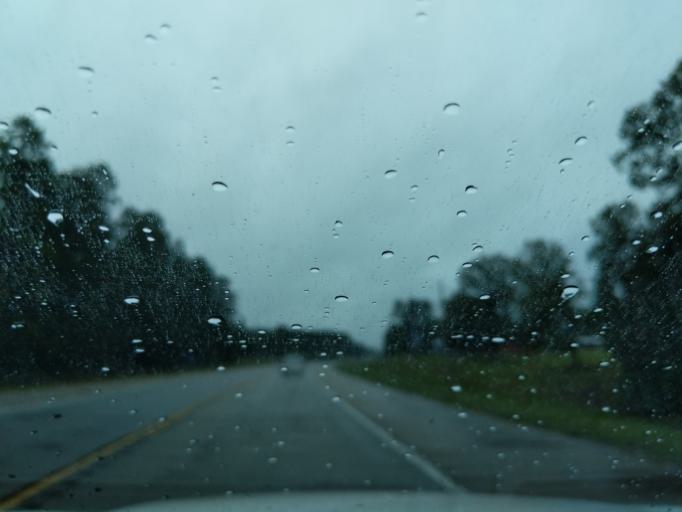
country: US
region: Louisiana
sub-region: Webster Parish
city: Minden
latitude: 32.5926
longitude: -93.2481
